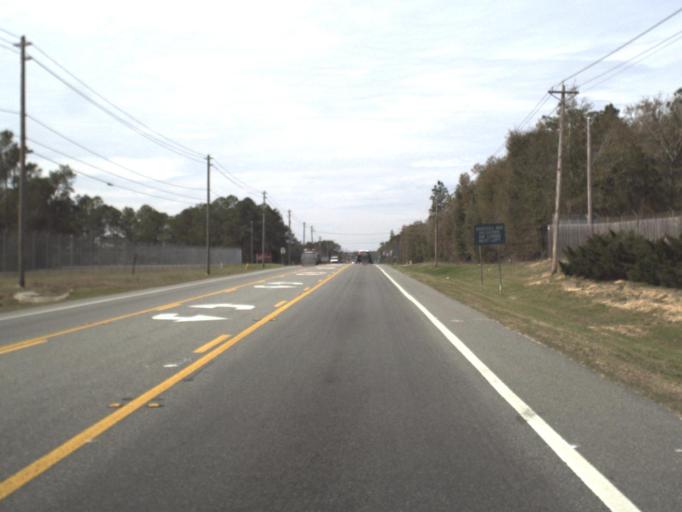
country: US
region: Florida
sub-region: Leon County
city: Tallahassee
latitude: 30.3980
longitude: -84.3346
